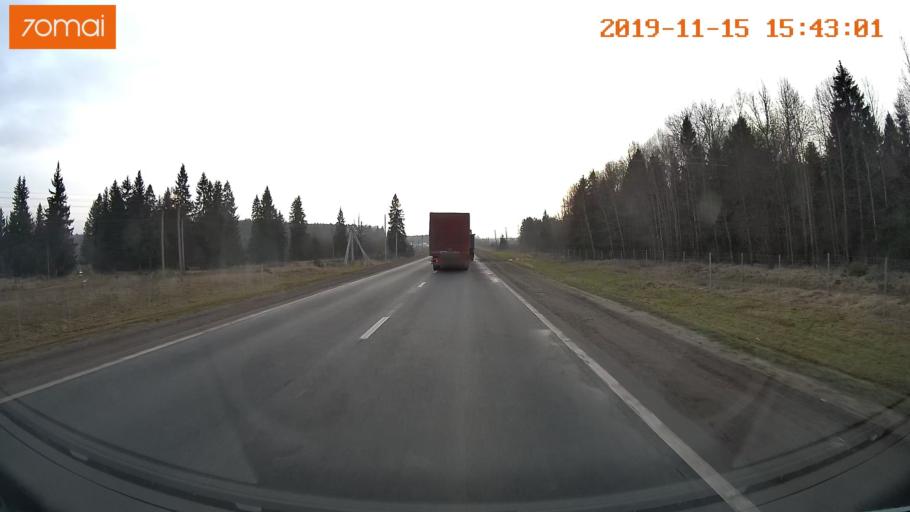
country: RU
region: Jaroslavl
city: Danilov
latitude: 57.9870
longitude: 40.0325
